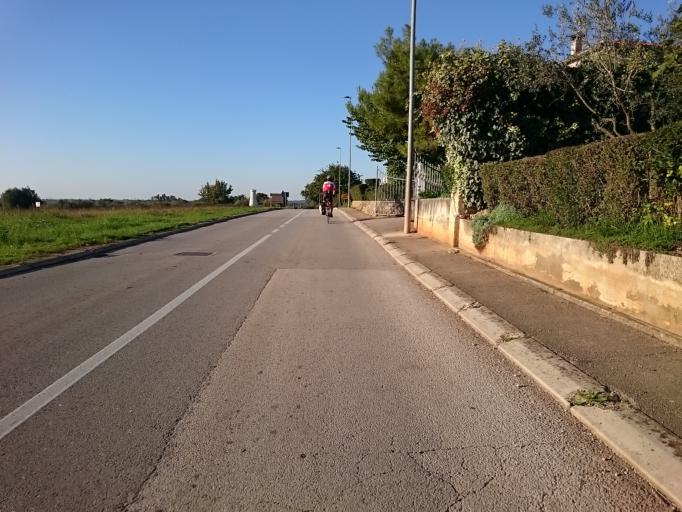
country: HR
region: Istarska
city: Novigrad
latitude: 45.3059
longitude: 13.6238
